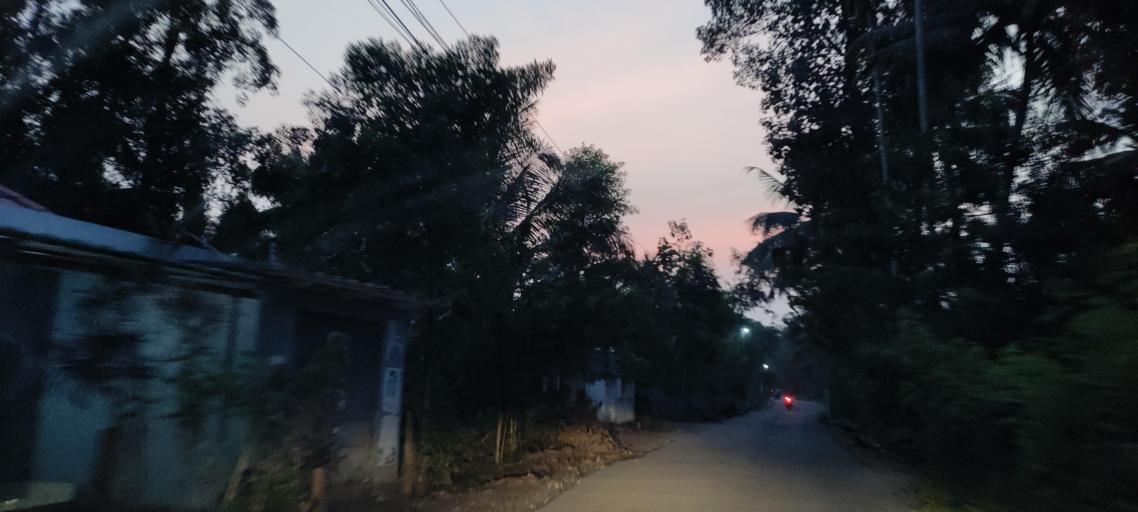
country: IN
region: Kerala
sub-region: Alappuzha
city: Mavelikara
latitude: 9.3213
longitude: 76.4559
